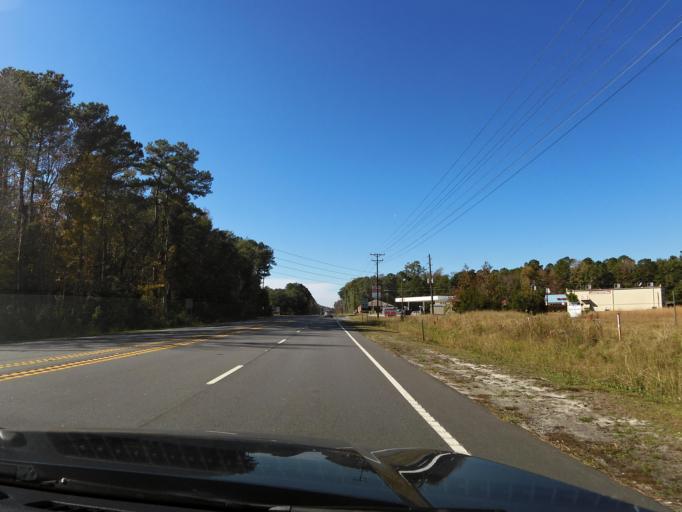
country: US
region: Georgia
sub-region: Liberty County
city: Midway
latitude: 31.7999
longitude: -81.4181
